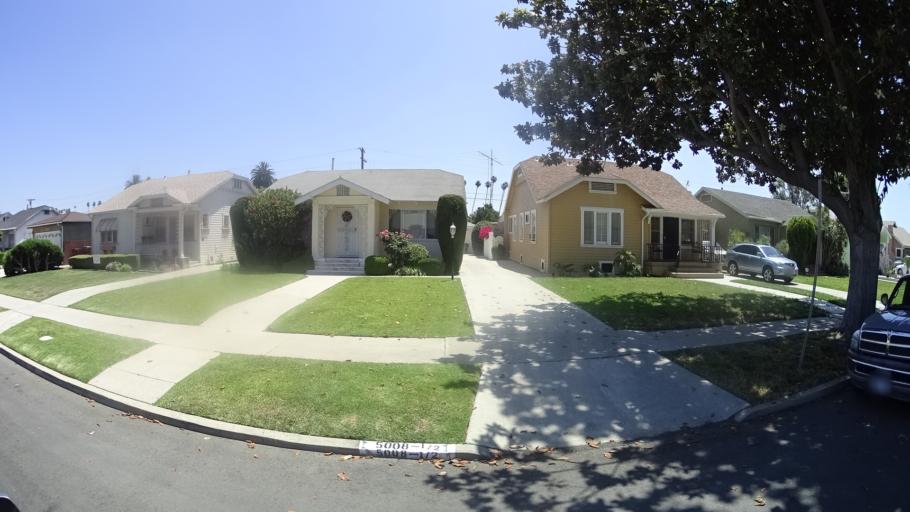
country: US
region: California
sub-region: Los Angeles County
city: View Park-Windsor Hills
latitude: 33.9976
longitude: -118.3225
